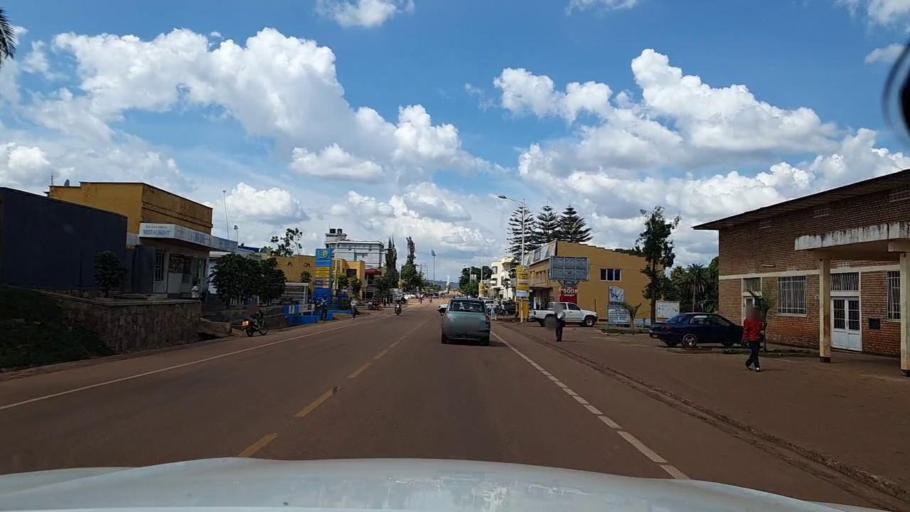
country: RW
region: Southern Province
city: Butare
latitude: -2.6039
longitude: 29.7413
